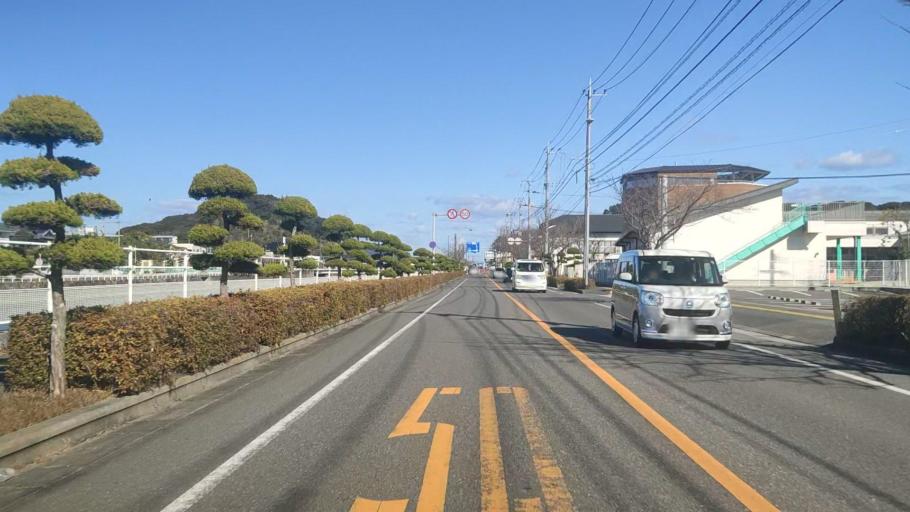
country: JP
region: Oita
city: Saiki
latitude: 32.9538
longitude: 131.9074
